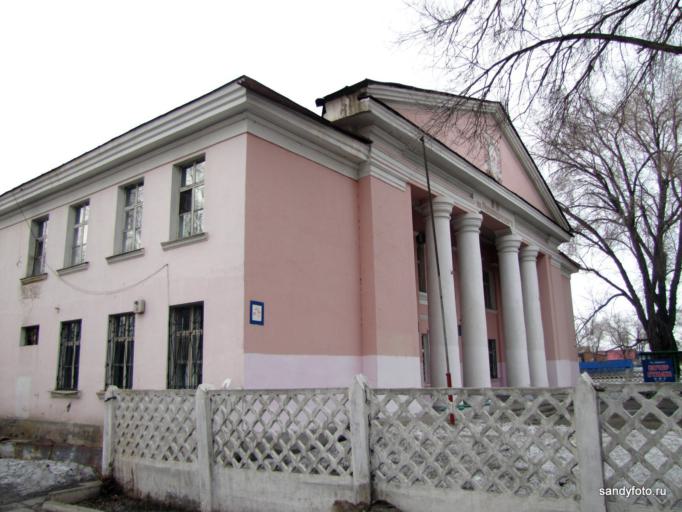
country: RU
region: Chelyabinsk
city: Troitsk
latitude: 54.1120
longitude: 61.5669
